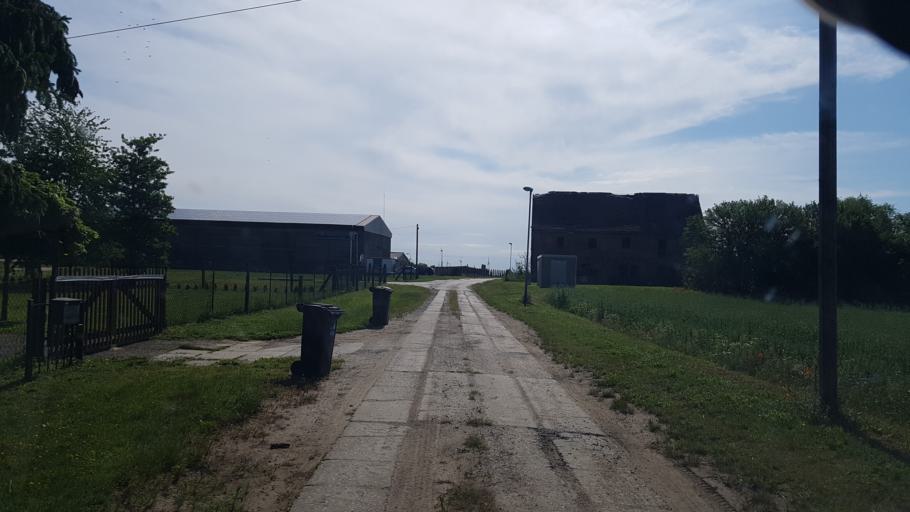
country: DE
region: Brandenburg
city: Gramzow
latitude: 53.2615
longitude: 13.9734
